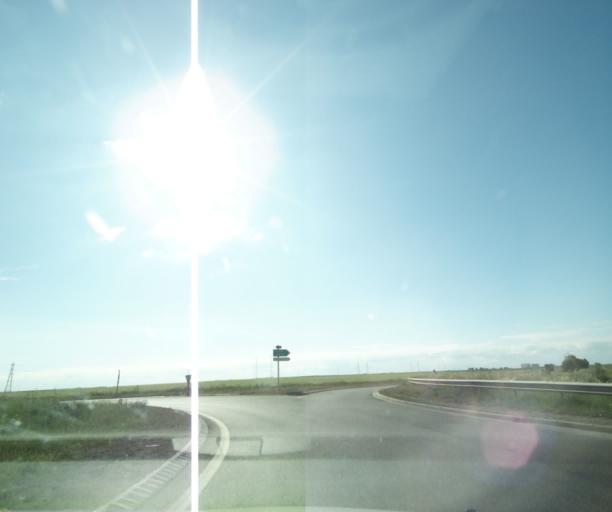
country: FR
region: Centre
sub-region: Departement d'Eure-et-Loir
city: Janville
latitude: 48.2076
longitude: 1.8211
